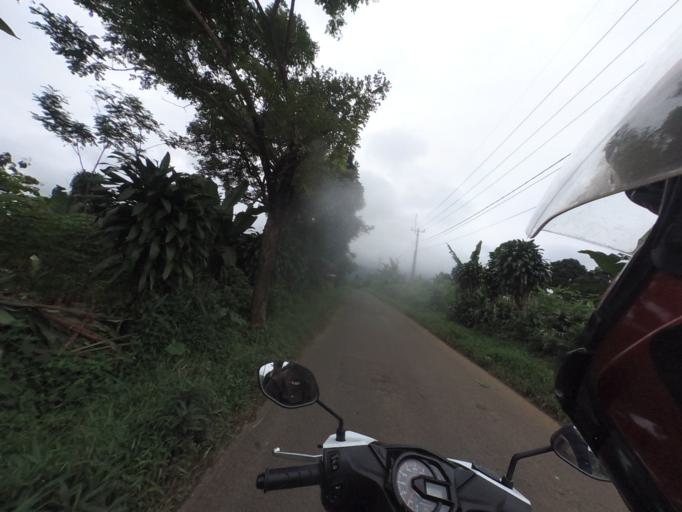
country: ID
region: West Java
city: Bogor
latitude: -6.6514
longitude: 106.7278
